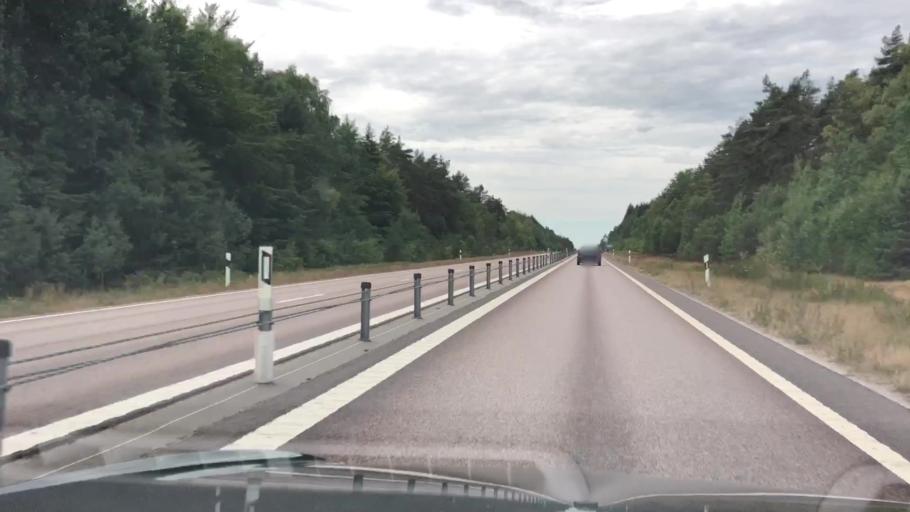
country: SE
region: Blekinge
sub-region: Karlskrona Kommun
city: Jaemjoe
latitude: 56.2069
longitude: 15.8690
